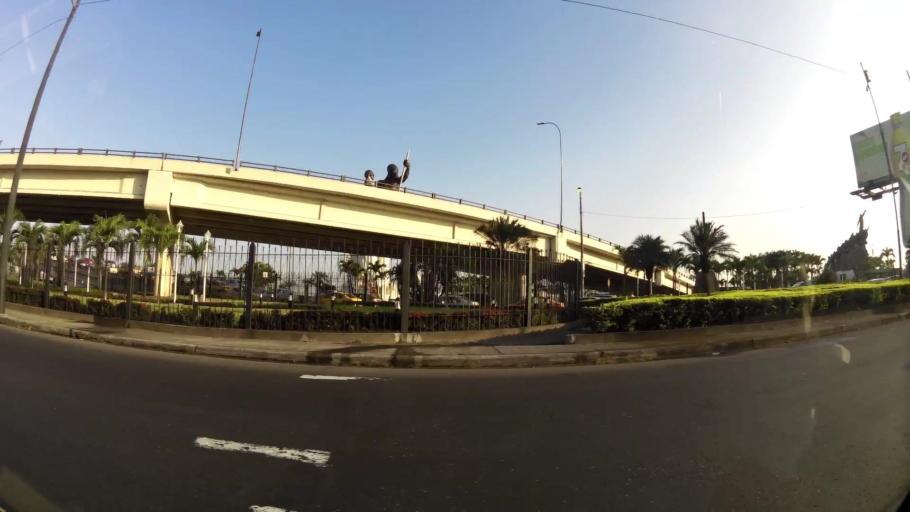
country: EC
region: Guayas
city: Eloy Alfaro
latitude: -2.1553
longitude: -79.8788
